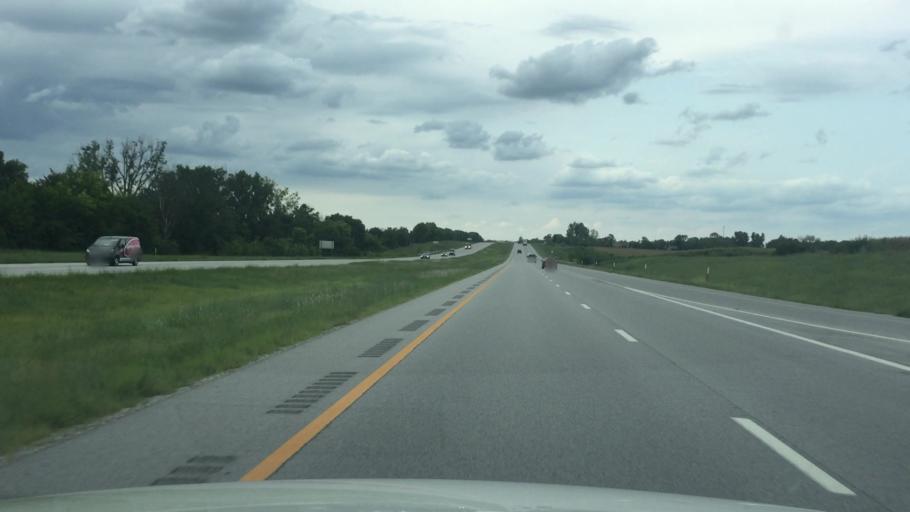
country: US
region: Kansas
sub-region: Miami County
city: Louisburg
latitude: 38.7253
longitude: -94.6761
